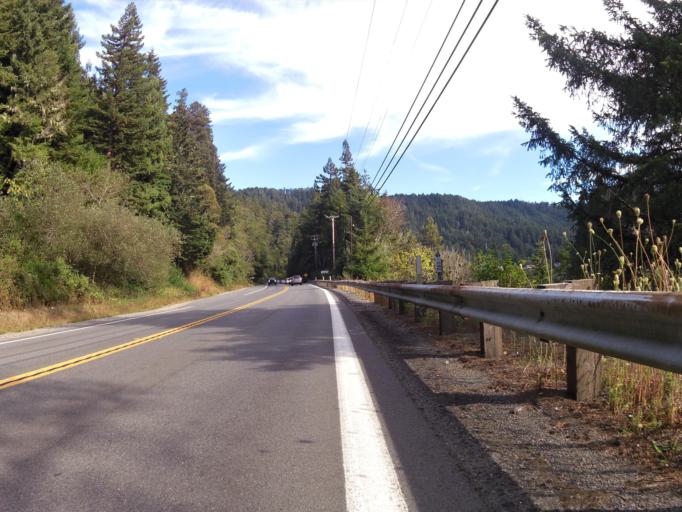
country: US
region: California
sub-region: Del Norte County
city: Bertsch-Oceanview
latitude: 41.8150
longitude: -124.0872
